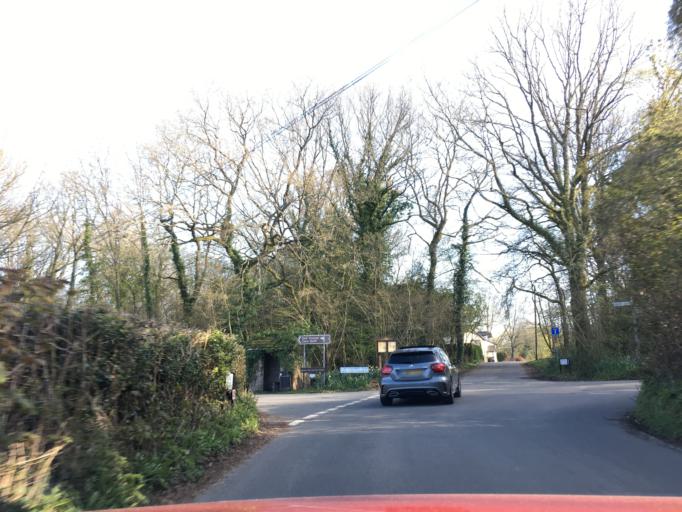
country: GB
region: Wales
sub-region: Torfaen County Borough
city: New Inn
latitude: 51.7070
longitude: -2.9671
